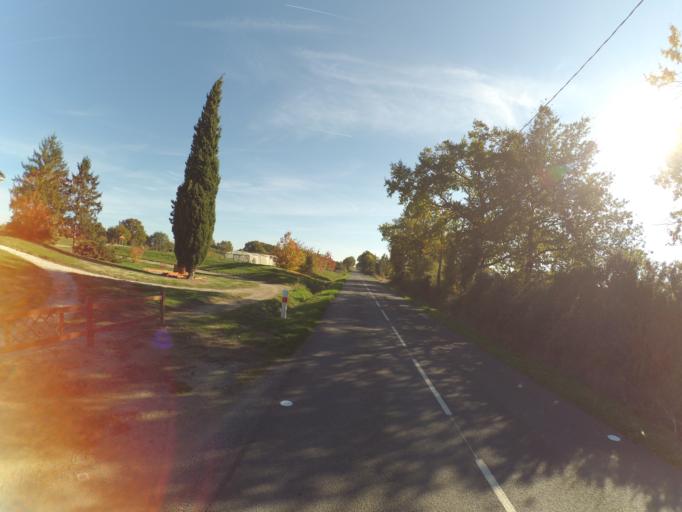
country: FR
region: Pays de la Loire
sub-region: Departement de la Loire-Atlantique
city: Saint-Lumine-de-Clisson
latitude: 47.0805
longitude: -1.3314
